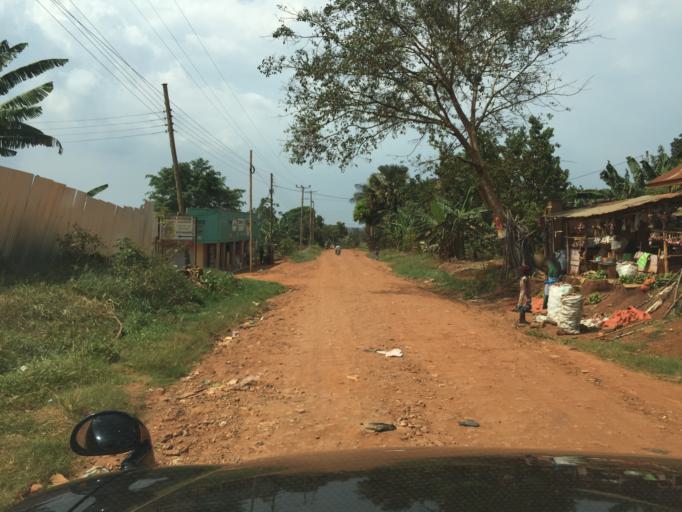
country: UG
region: Central Region
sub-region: Wakiso District
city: Kireka
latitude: 0.4084
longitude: 32.6200
